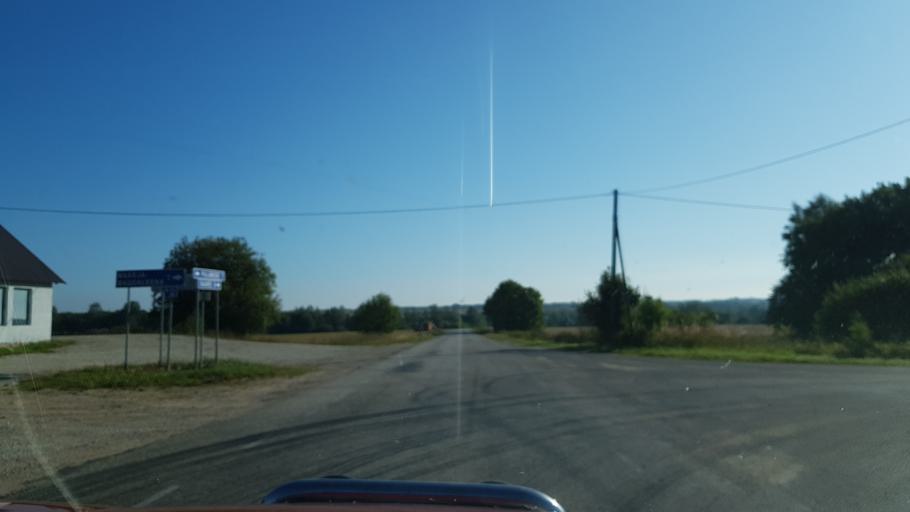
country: EE
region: Jogevamaa
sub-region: Tabivere vald
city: Tabivere
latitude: 58.6715
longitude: 26.6967
